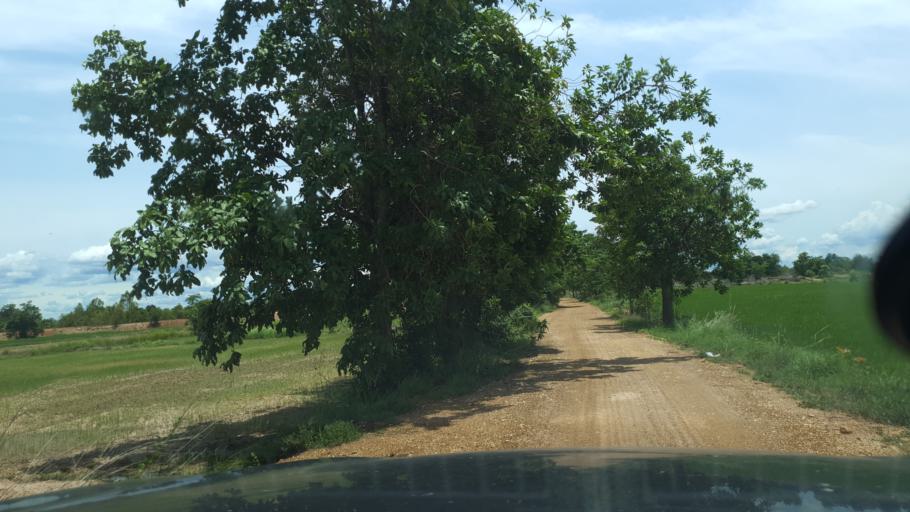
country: TH
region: Sukhothai
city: Ban Na
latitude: 17.1345
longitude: 99.6701
